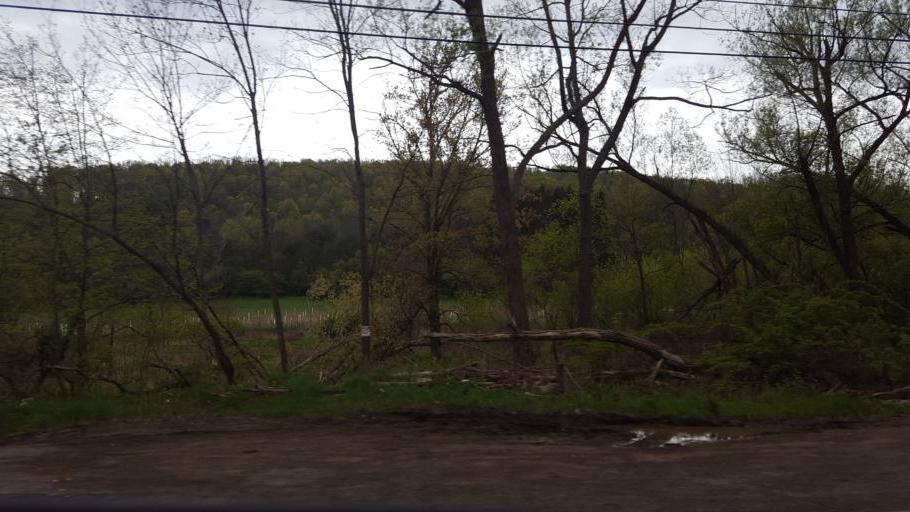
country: US
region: Pennsylvania
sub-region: Tioga County
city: Westfield
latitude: 41.9158
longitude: -77.6140
